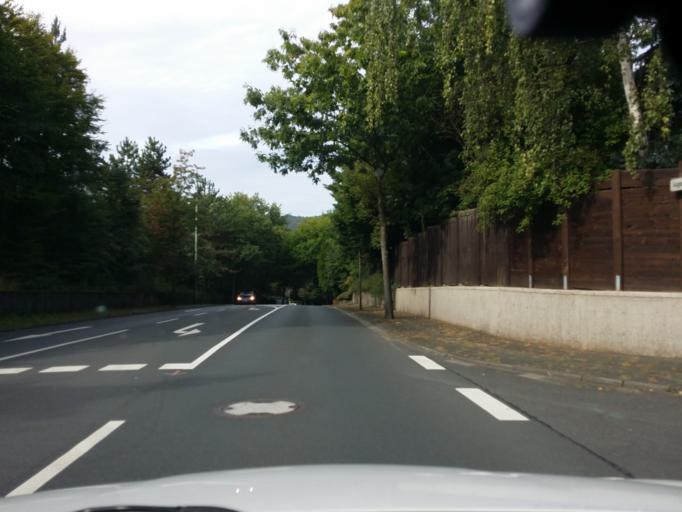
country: DE
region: Hesse
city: Kelkheim (Taunus)
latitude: 50.1498
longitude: 8.4558
